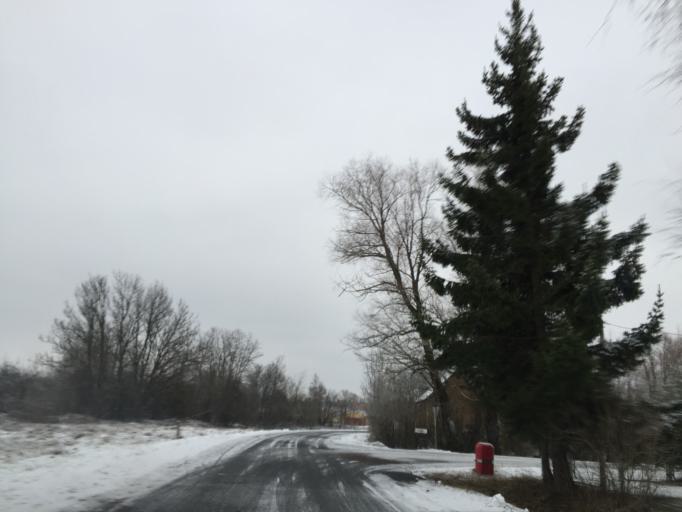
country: EE
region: Laeaene
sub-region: Lihula vald
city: Lihula
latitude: 58.6806
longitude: 23.8376
